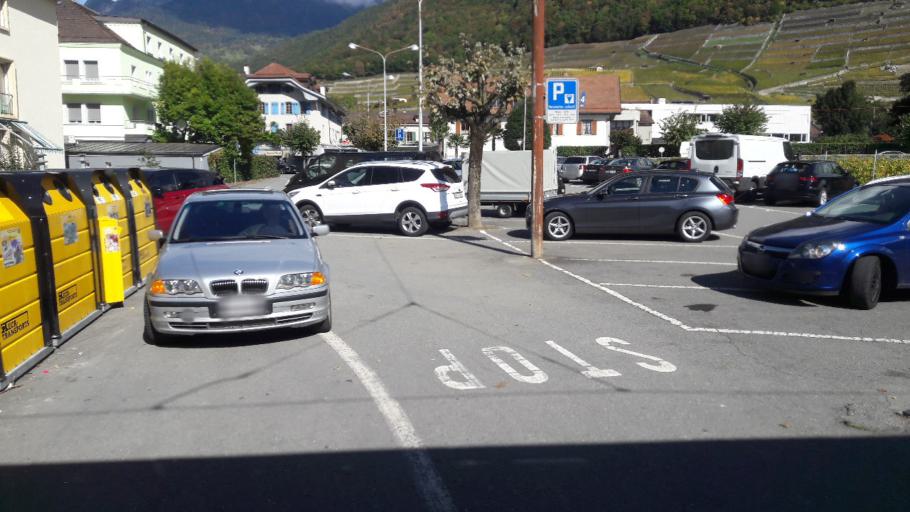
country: CH
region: Vaud
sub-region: Aigle District
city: Aigle
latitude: 46.3166
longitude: 6.9706
